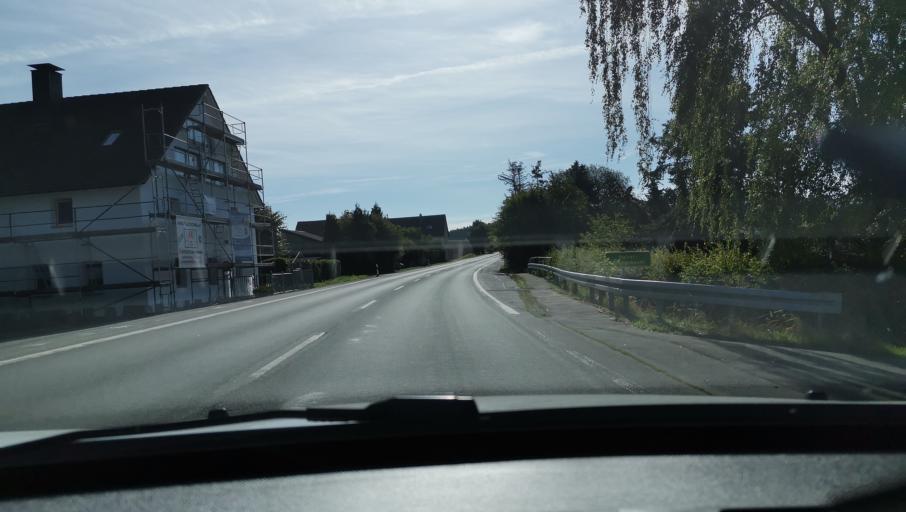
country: DE
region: North Rhine-Westphalia
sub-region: Regierungsbezirk Arnsberg
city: Breckerfeld
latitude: 51.2257
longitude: 7.4809
